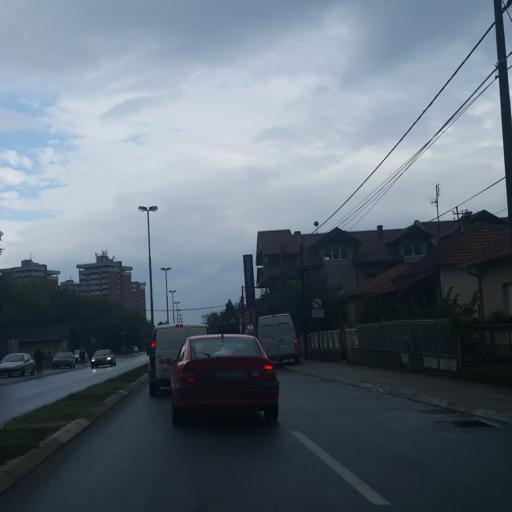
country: RS
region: Central Serbia
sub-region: Rasinski Okrug
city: Krusevac
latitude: 43.5720
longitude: 21.3409
